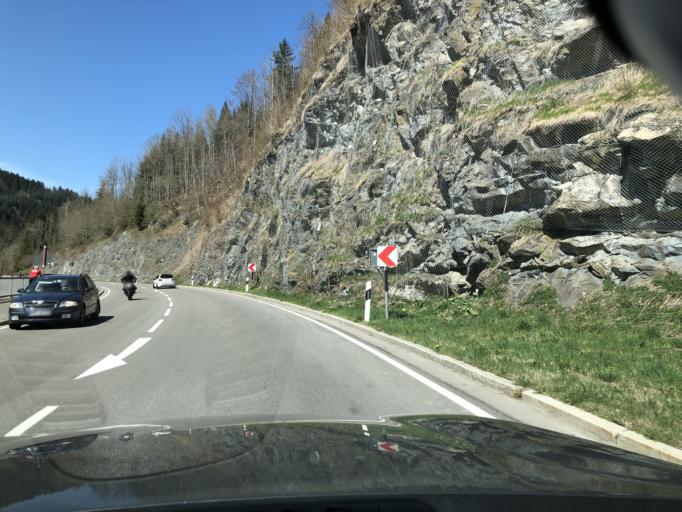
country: DE
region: Bavaria
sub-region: Swabia
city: Wertach
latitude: 47.5823
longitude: 10.4196
